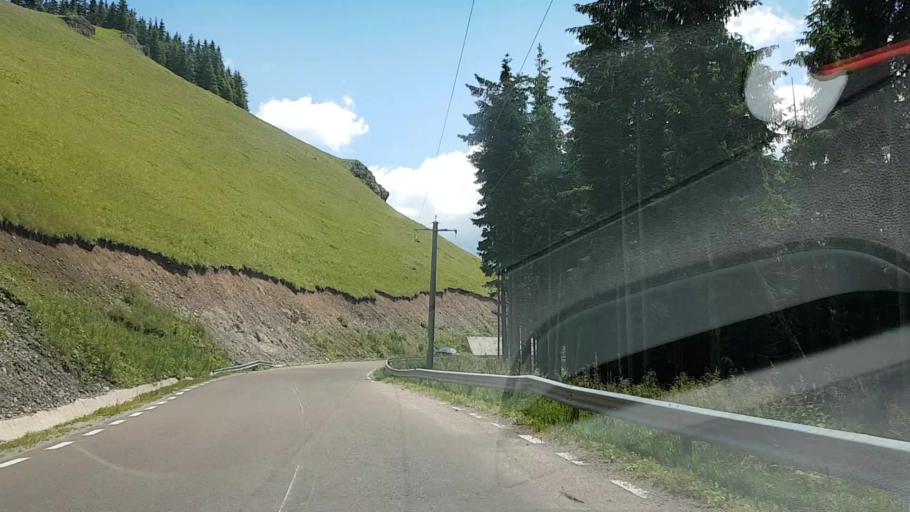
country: RO
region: Suceava
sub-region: Municipiul Campulung Moldovenesc
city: Campulung Moldovenesc
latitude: 47.4545
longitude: 25.5407
